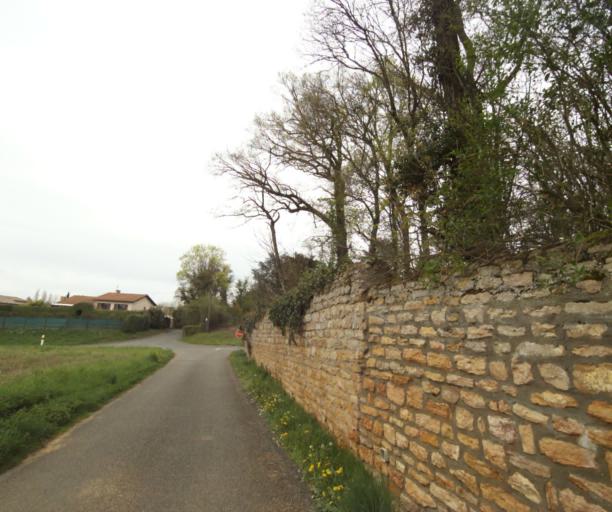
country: FR
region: Bourgogne
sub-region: Departement de Saone-et-Loire
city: Charnay-les-Macon
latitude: 46.2986
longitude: 4.7780
